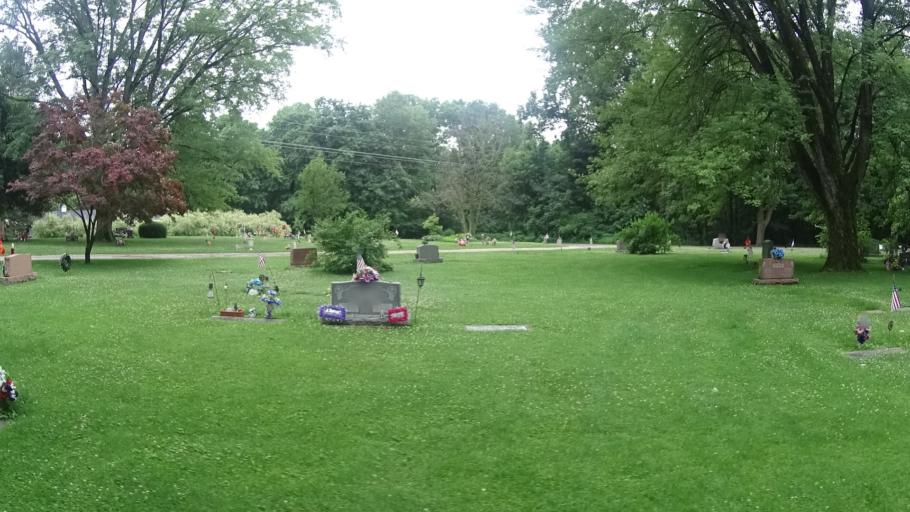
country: US
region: Ohio
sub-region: Erie County
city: Huron
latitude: 41.3184
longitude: -82.4950
